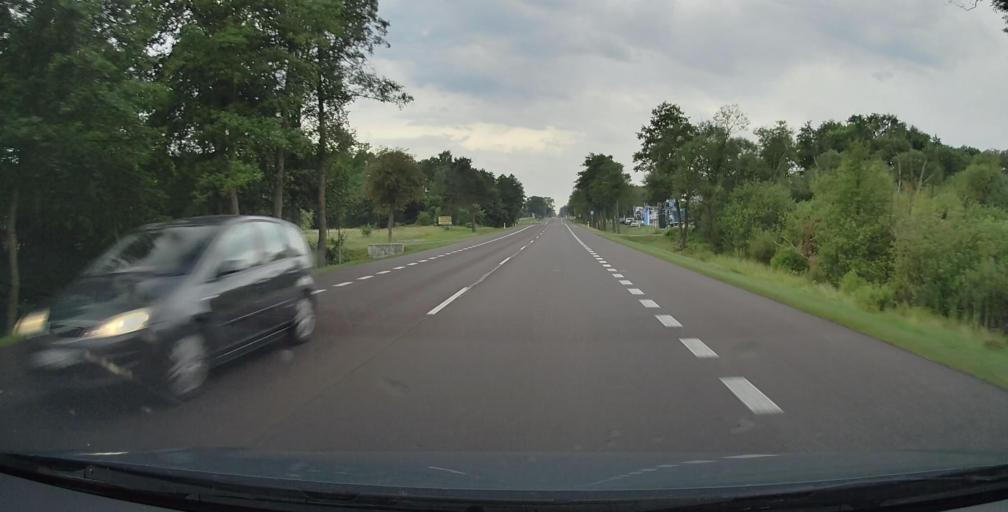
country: PL
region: Lublin Voivodeship
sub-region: Powiat bialski
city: Miedzyrzec Podlaski
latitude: 52.0037
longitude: 22.8220
